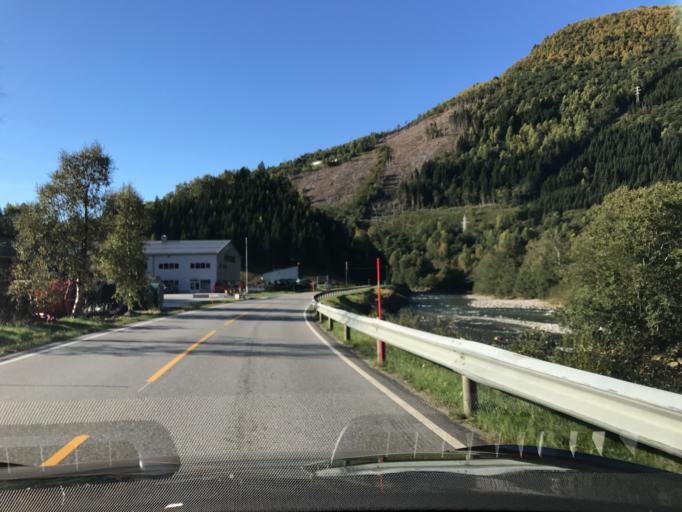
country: NO
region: More og Romsdal
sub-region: Norddal
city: Valldal
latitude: 62.3081
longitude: 7.2607
